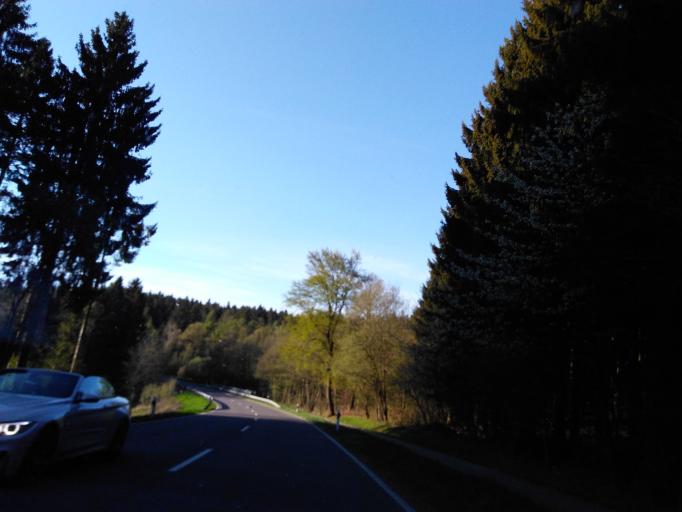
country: DE
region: North Rhine-Westphalia
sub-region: Regierungsbezirk Koln
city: Engelskirchen
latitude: 50.9607
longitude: 7.4595
